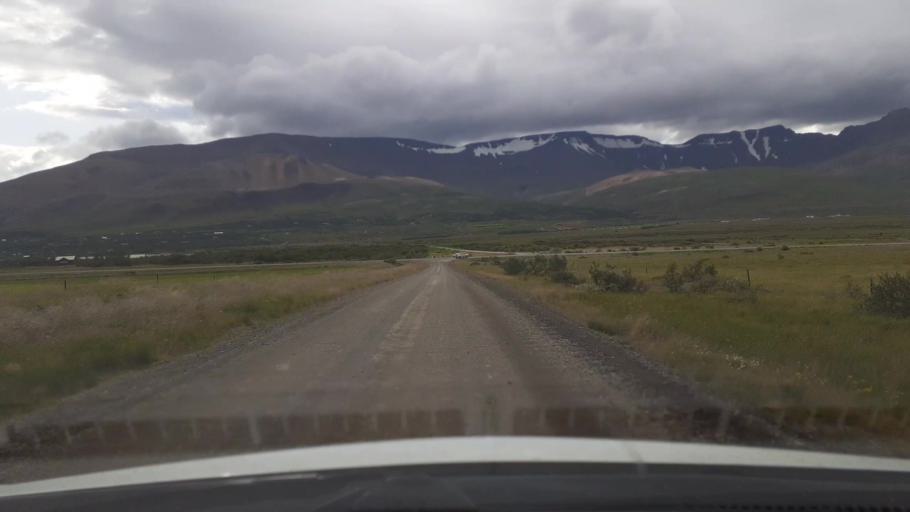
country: IS
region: West
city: Borgarnes
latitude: 64.5452
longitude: -21.6195
